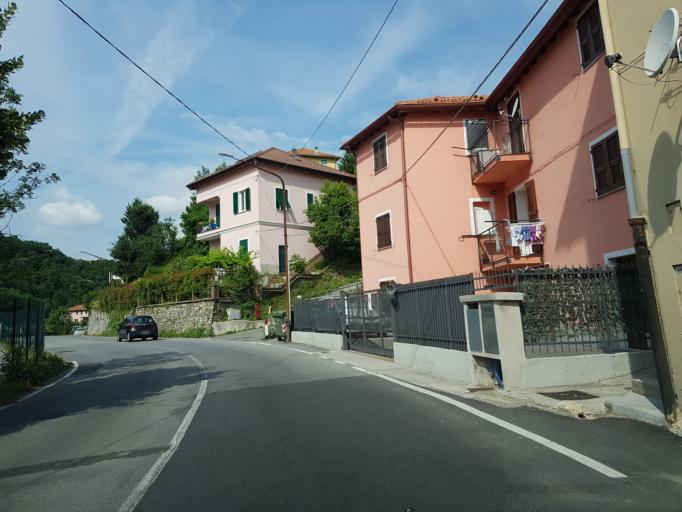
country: IT
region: Liguria
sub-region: Provincia di Genova
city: Manesseno
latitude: 44.4782
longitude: 8.9320
